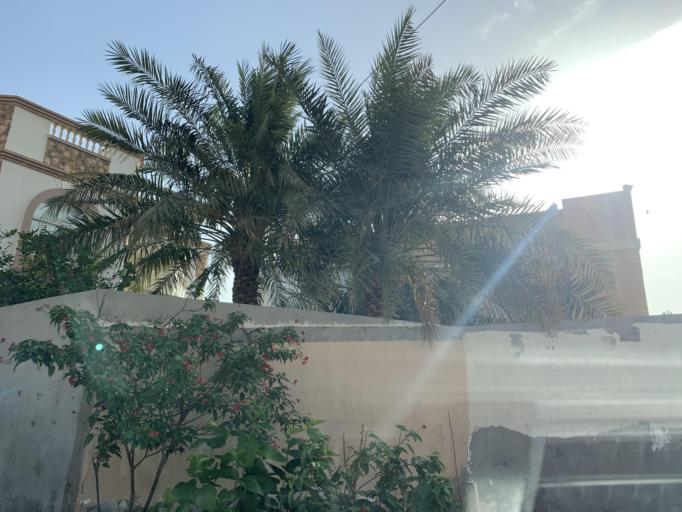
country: BH
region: Manama
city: Manama
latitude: 26.1815
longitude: 50.5833
